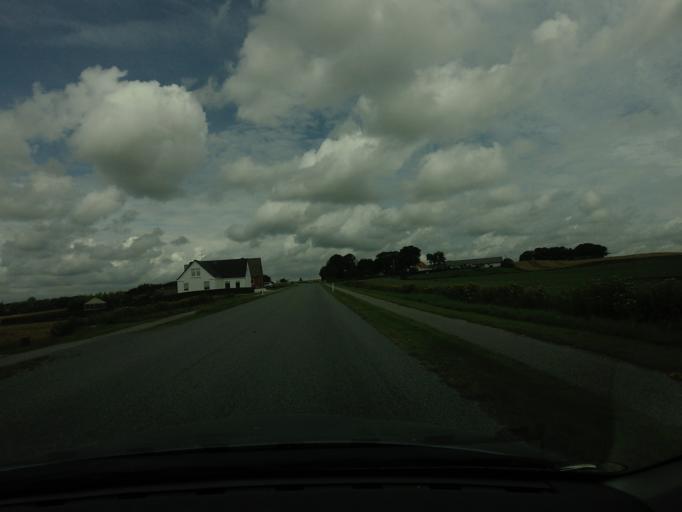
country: DK
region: North Denmark
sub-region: Hjorring Kommune
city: Tars
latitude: 57.3503
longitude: 10.2261
